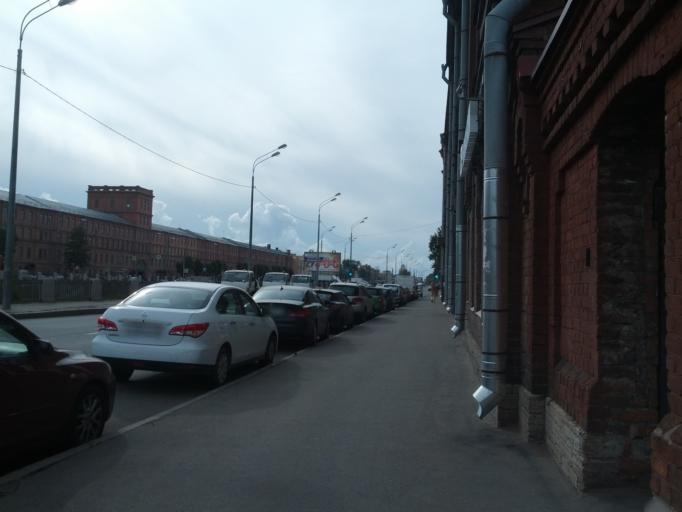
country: RU
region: St.-Petersburg
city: Admiralteisky
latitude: 59.9095
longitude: 30.2844
